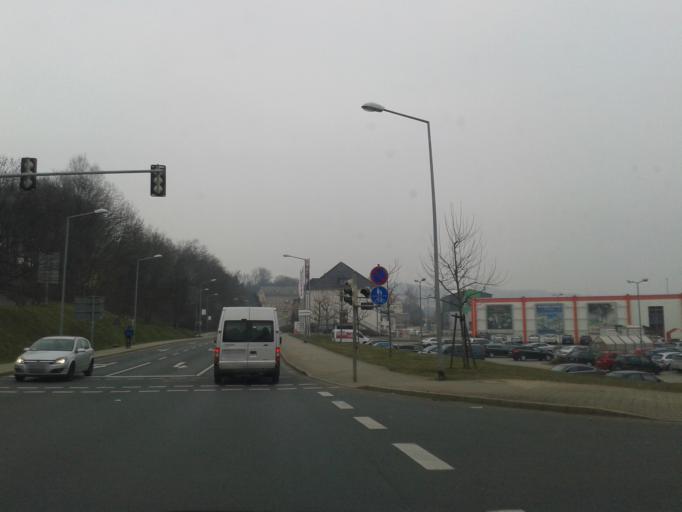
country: DE
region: Saxony
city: Freital
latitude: 51.0039
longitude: 13.6473
